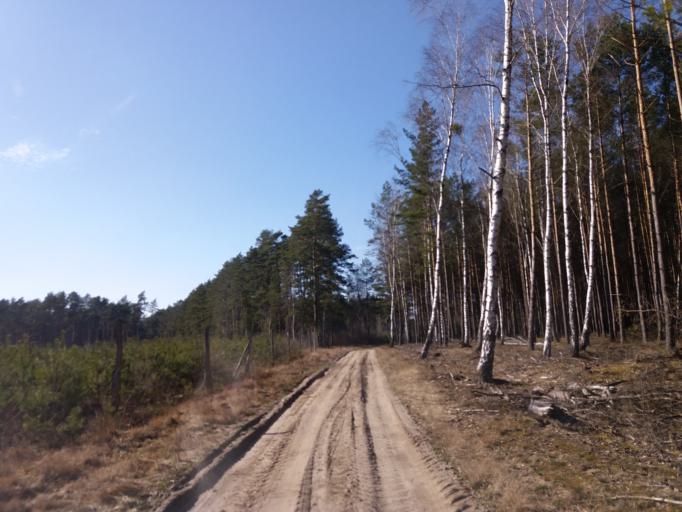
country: PL
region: West Pomeranian Voivodeship
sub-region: Powiat choszczenski
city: Bierzwnik
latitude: 53.1039
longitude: 15.7071
